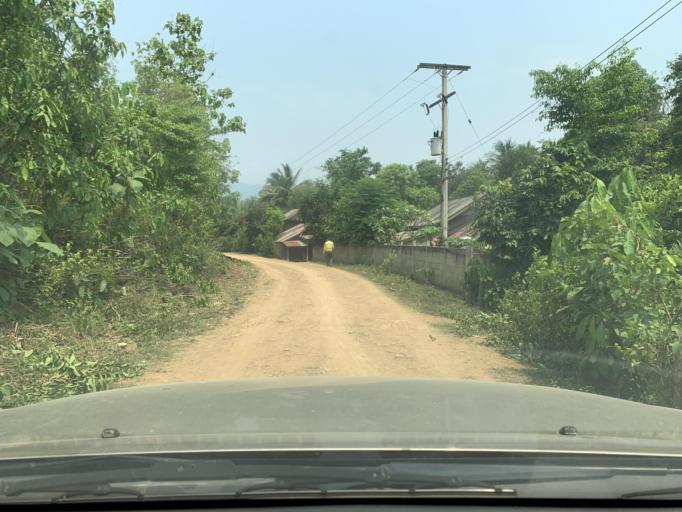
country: LA
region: Louangphabang
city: Louangphabang
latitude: 19.9457
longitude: 102.1342
